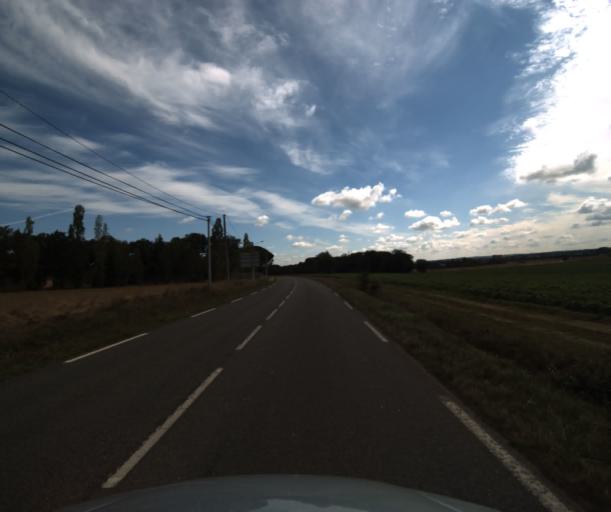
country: FR
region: Midi-Pyrenees
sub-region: Departement de la Haute-Garonne
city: Seysses
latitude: 43.4596
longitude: 1.2948
